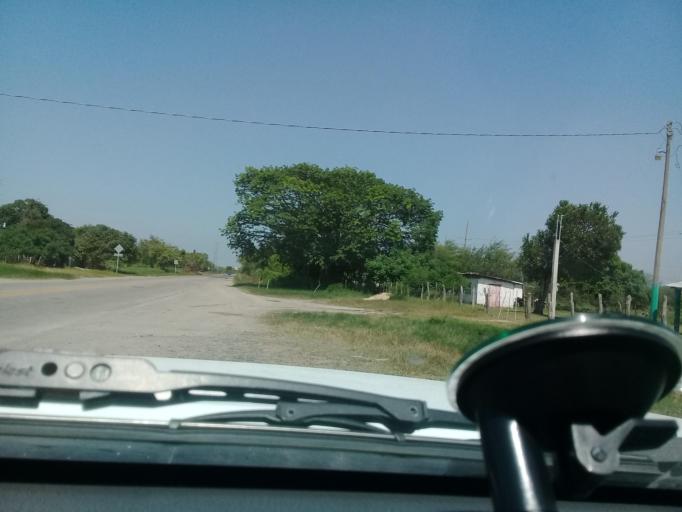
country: MX
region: Veracruz
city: Moralillo
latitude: 22.1714
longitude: -98.0476
